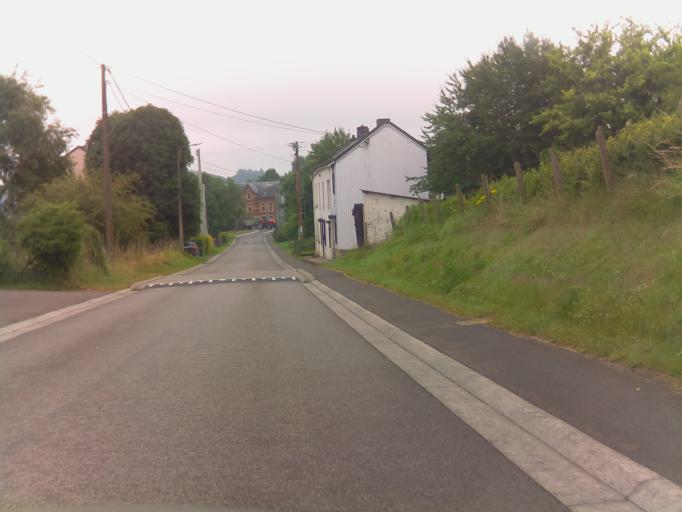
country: BE
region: Wallonia
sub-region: Province du Luxembourg
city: Neufchateau
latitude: 49.8574
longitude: 5.4508
